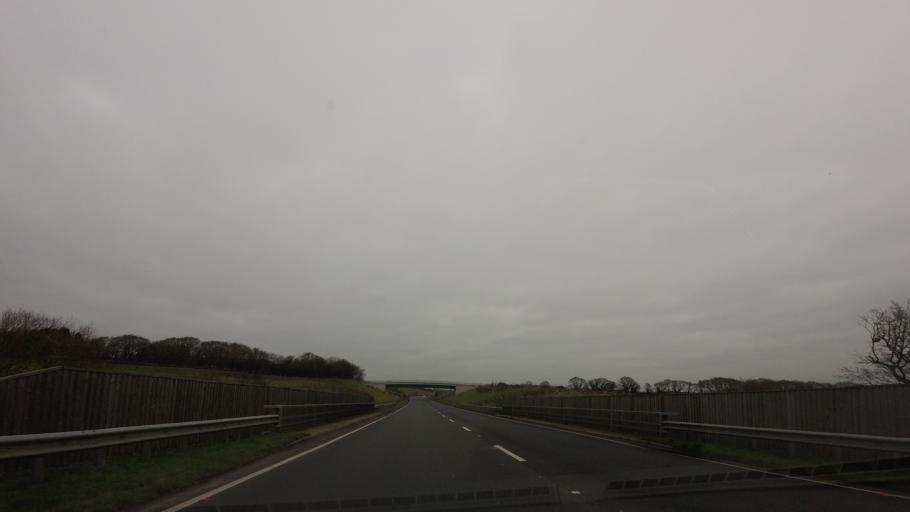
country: GB
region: England
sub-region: East Sussex
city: Bexhill-on-Sea
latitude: 50.8630
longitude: 0.4830
